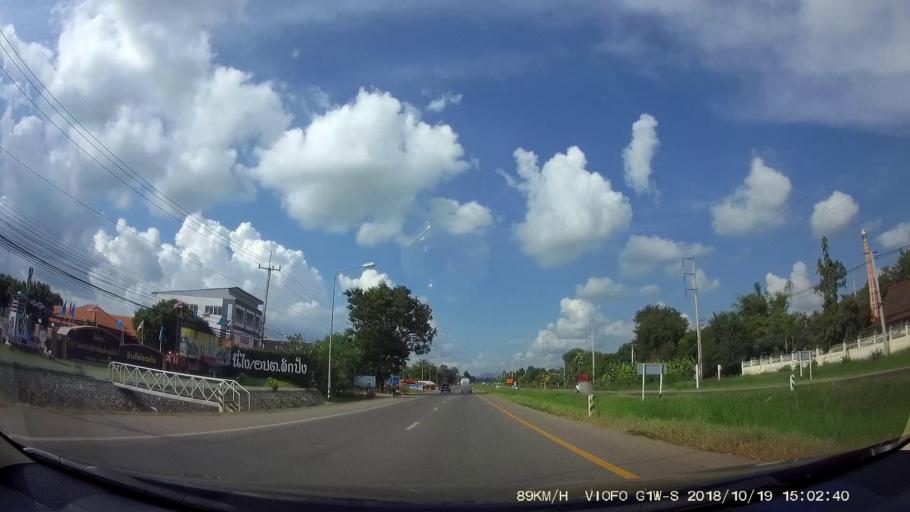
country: TH
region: Chaiyaphum
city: Phu Khiao
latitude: 16.4018
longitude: 102.1312
